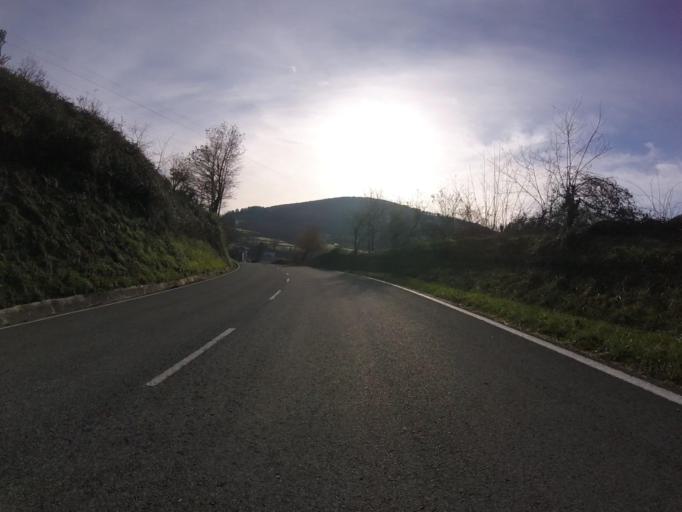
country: ES
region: Navarre
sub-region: Provincia de Navarra
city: Areso
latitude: 43.0926
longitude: -1.9408
